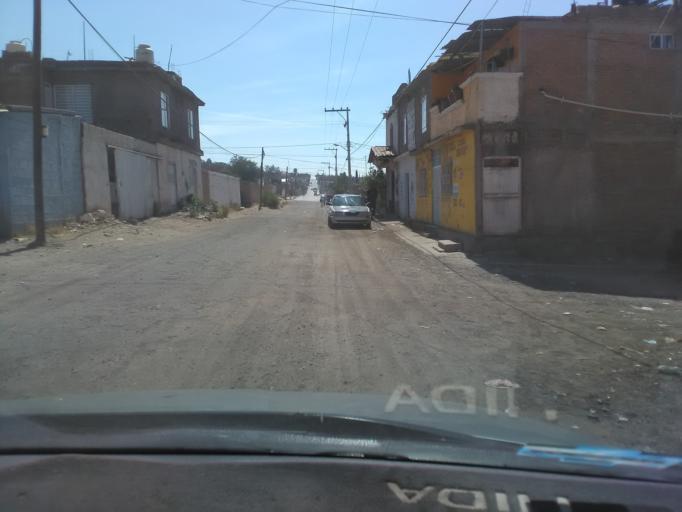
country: MX
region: Durango
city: Victoria de Durango
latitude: 24.0303
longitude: -104.7094
